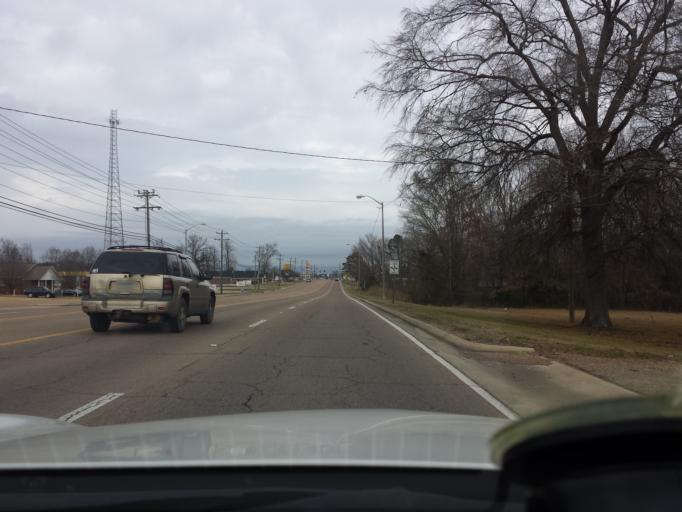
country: US
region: Mississippi
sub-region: Clay County
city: West Point
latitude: 33.6229
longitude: -88.6589
